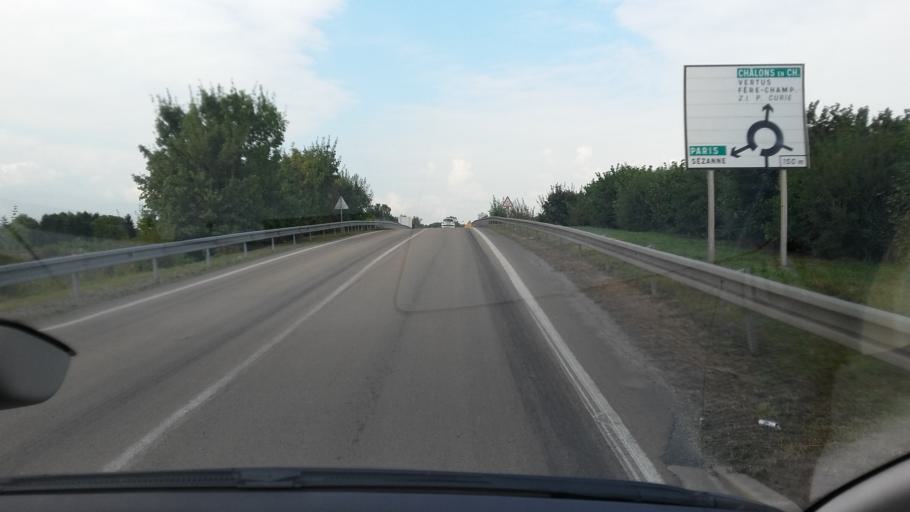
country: FR
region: Champagne-Ardenne
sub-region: Departement de la Marne
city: Fere-Champenoise
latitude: 48.7507
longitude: 4.0017
